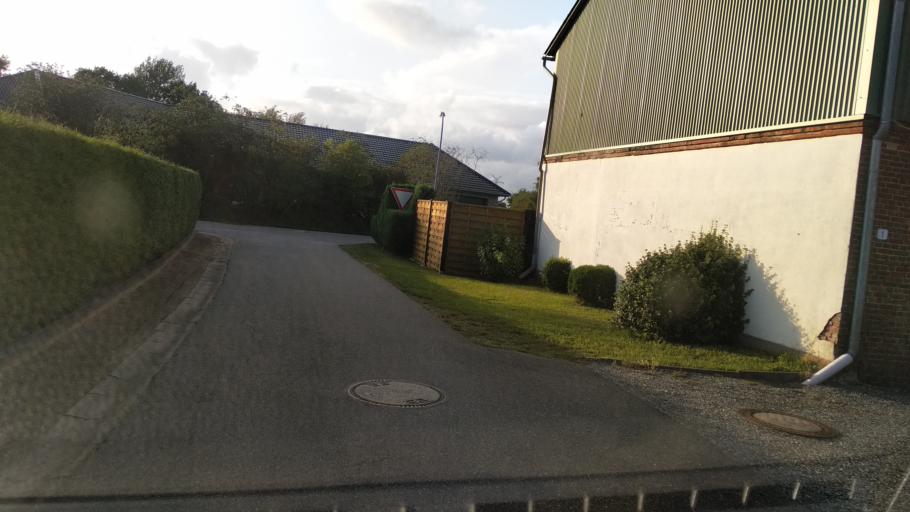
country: DE
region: Schleswig-Holstein
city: Klein Bennebek
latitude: 54.4024
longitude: 9.4583
